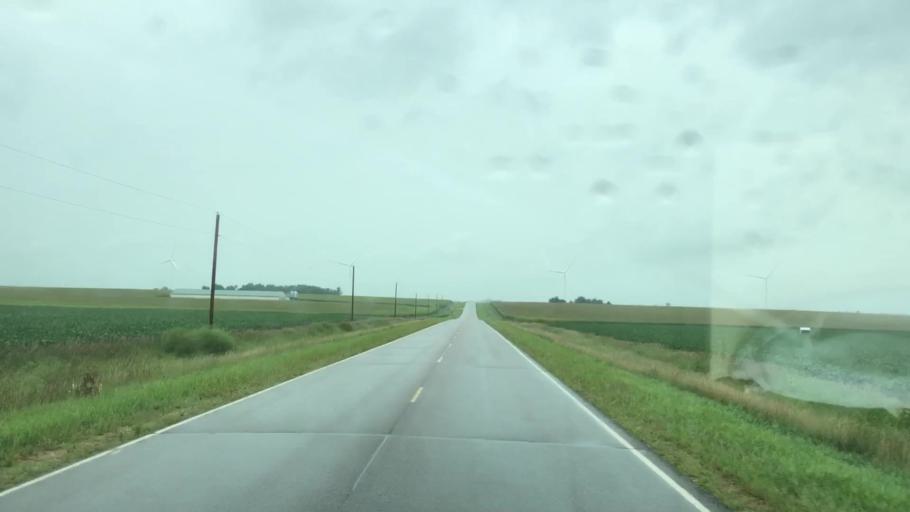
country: US
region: Iowa
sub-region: O'Brien County
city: Sanborn
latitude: 43.2109
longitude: -95.7233
